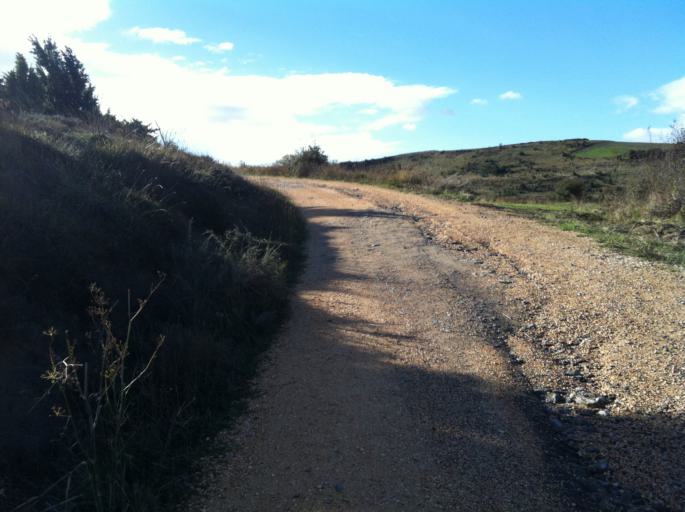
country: ES
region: Basque Country
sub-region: Provincia de Alava
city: Gasteiz / Vitoria
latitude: 42.8181
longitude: -2.6651
